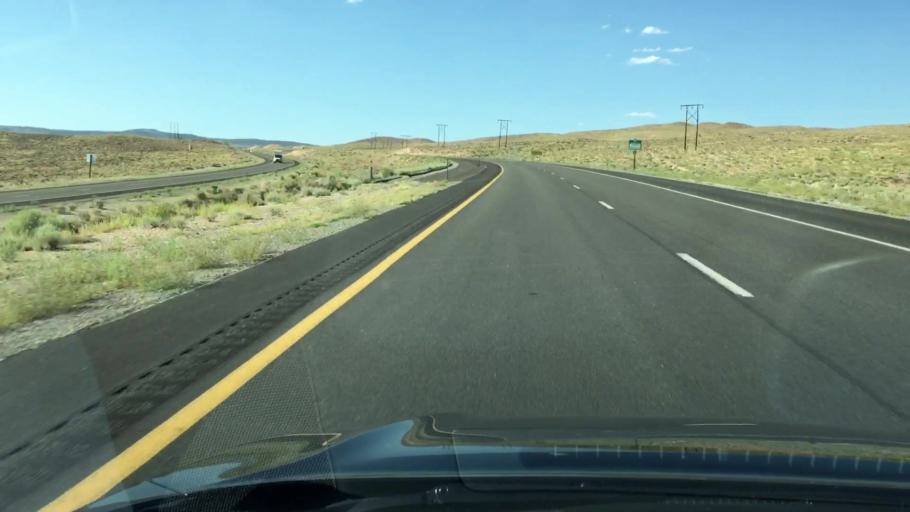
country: US
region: California
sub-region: Inyo County
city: West Bishop
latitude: 37.4481
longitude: -118.5725
